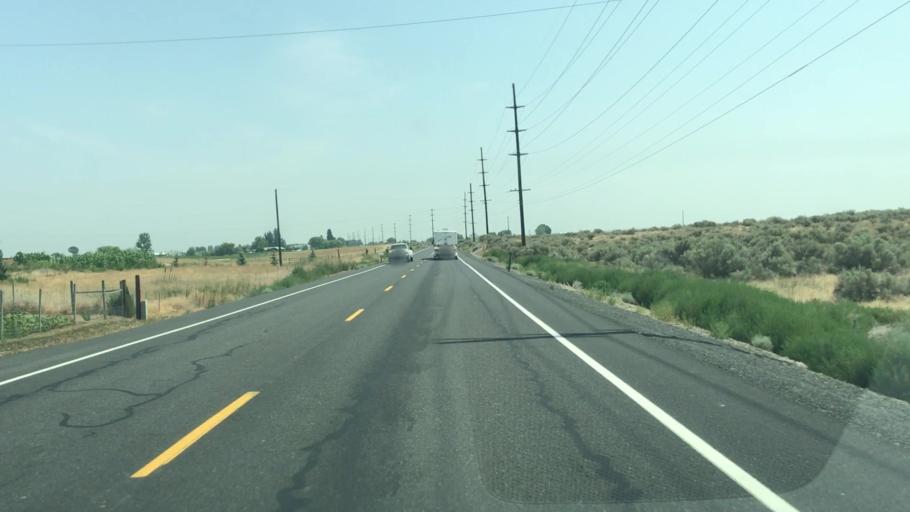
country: US
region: Washington
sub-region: Grant County
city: Quincy
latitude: 47.1601
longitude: -119.8913
